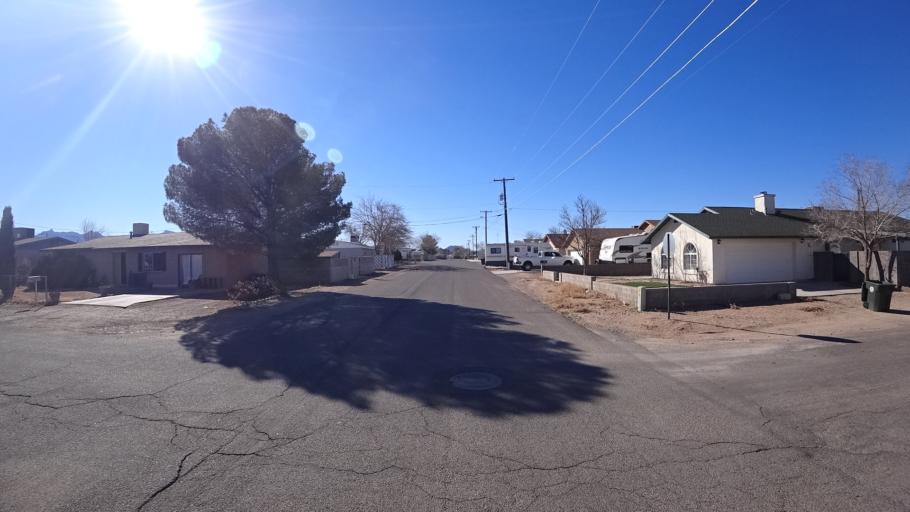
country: US
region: Arizona
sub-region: Mohave County
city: Kingman
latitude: 35.2060
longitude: -114.0270
